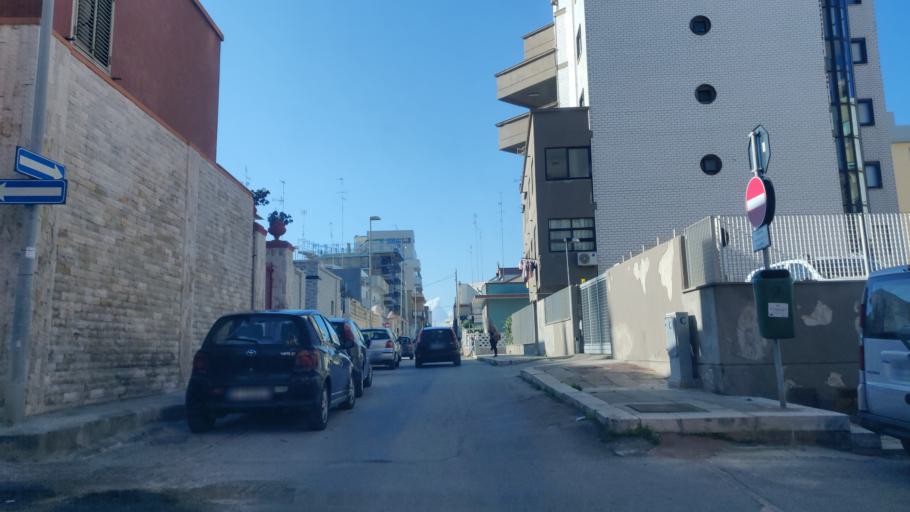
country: IT
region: Apulia
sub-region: Provincia di Bari
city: San Paolo
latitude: 41.1389
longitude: 16.8150
